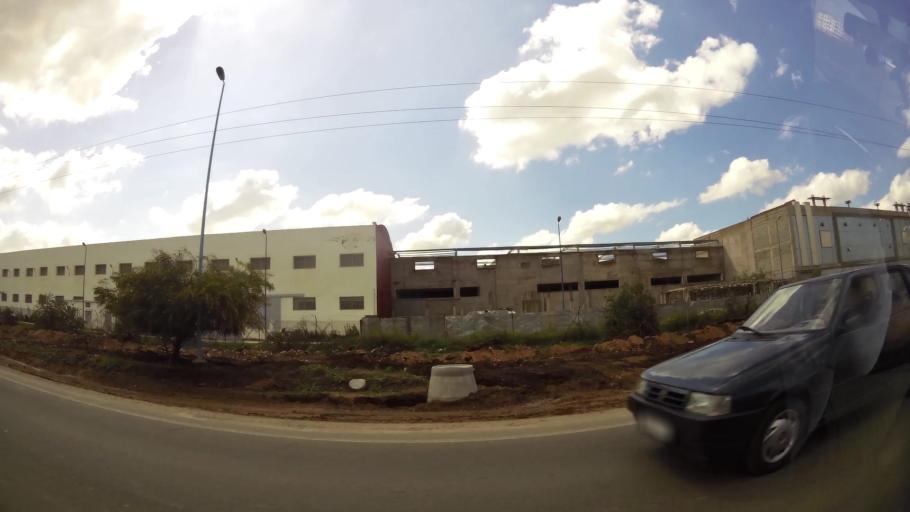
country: MA
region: Grand Casablanca
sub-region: Mediouna
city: Mediouna
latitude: 33.3919
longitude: -7.5355
